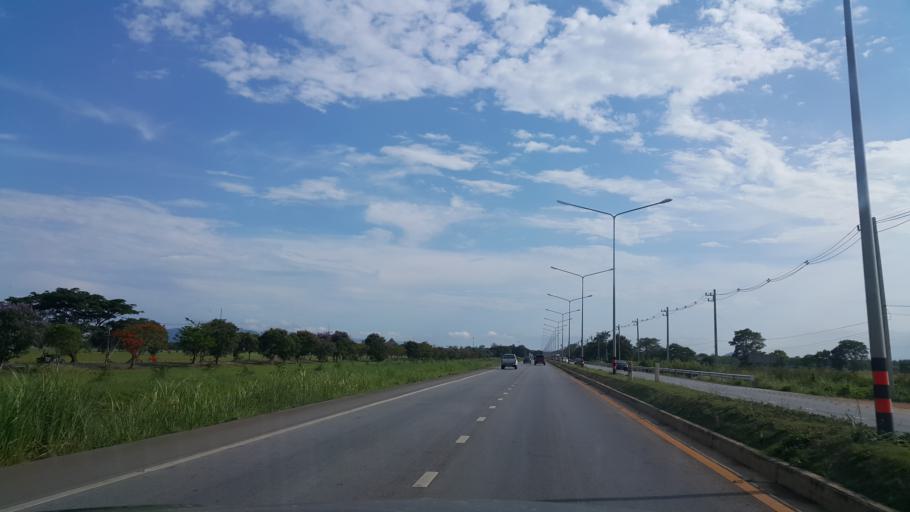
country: TH
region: Chiang Rai
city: Chiang Rai
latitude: 19.9416
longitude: 99.8693
